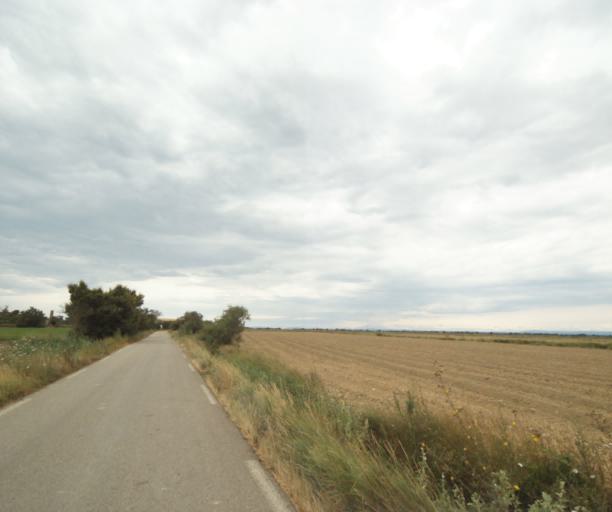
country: FR
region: Languedoc-Roussillon
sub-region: Departement de l'Herault
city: La Grande-Motte
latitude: 43.6014
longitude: 4.1280
